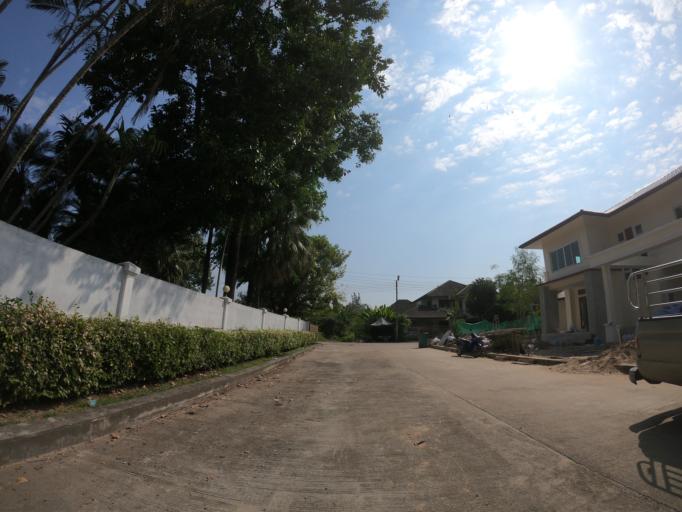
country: TH
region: Chiang Mai
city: Chiang Mai
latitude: 18.8070
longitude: 99.0079
